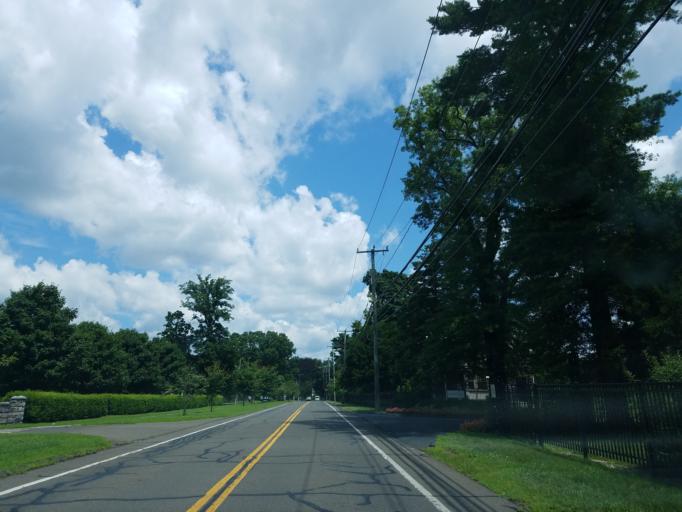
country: US
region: Connecticut
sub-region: Fairfield County
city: Darien
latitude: 41.0652
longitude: -73.4365
